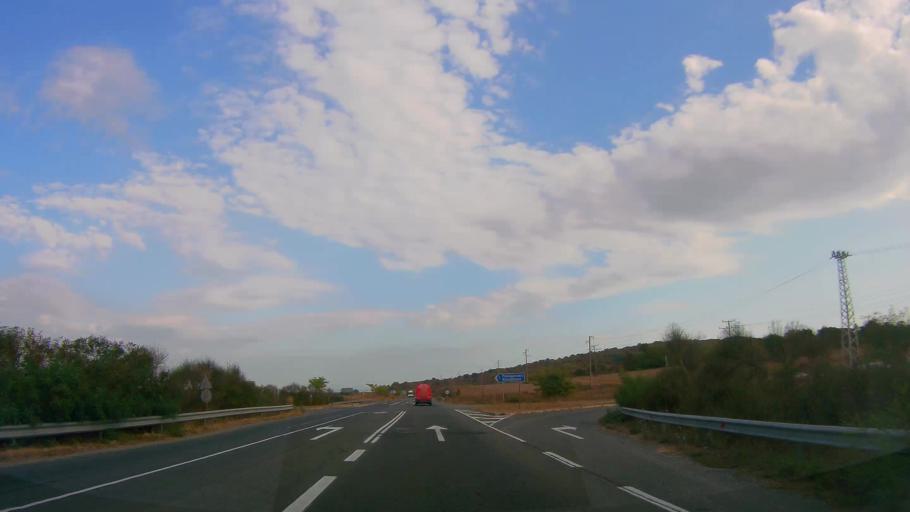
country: BG
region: Burgas
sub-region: Obshtina Sozopol
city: Sozopol
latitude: 42.3788
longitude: 27.6817
